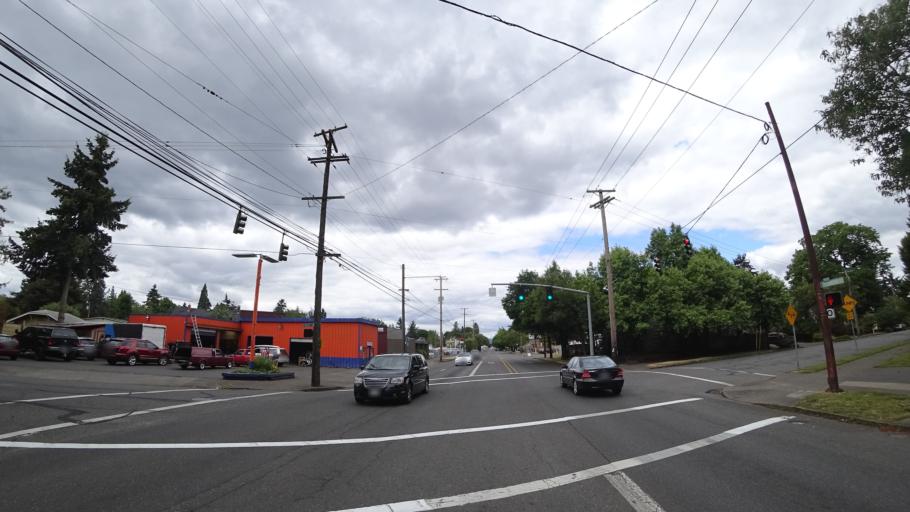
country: US
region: Oregon
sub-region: Multnomah County
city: Portland
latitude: 45.5785
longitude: -122.7133
